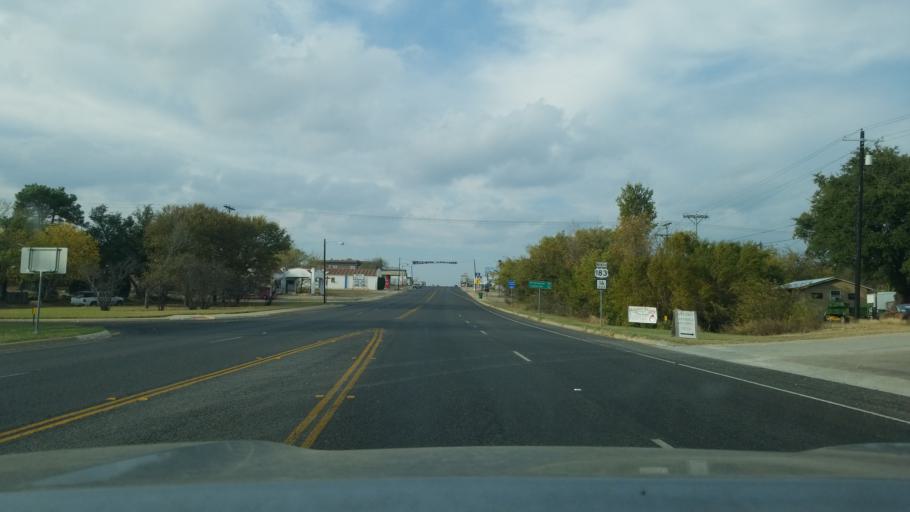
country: US
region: Texas
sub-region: Mills County
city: Goldthwaite
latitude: 31.4467
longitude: -98.5677
